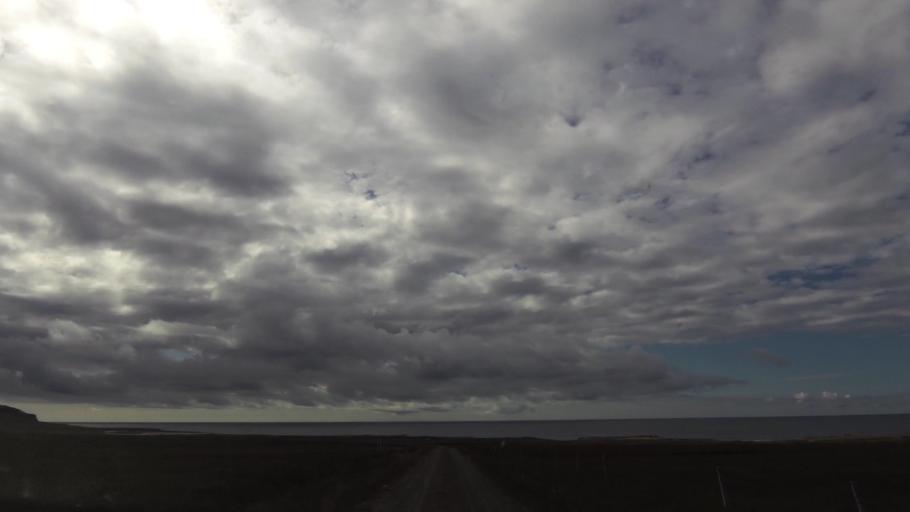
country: IS
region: West
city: Olafsvik
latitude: 65.6143
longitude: -24.3190
